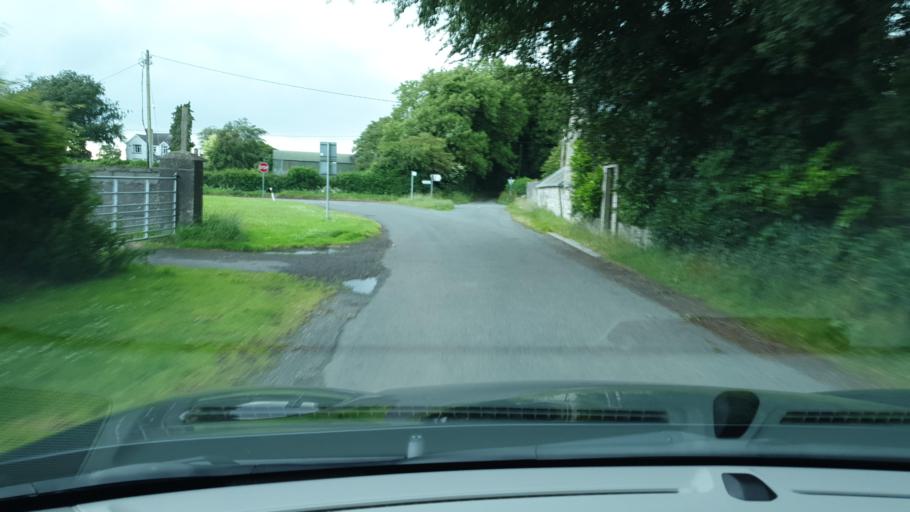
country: IE
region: Leinster
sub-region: An Mhi
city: Navan
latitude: 53.5912
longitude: -6.6245
